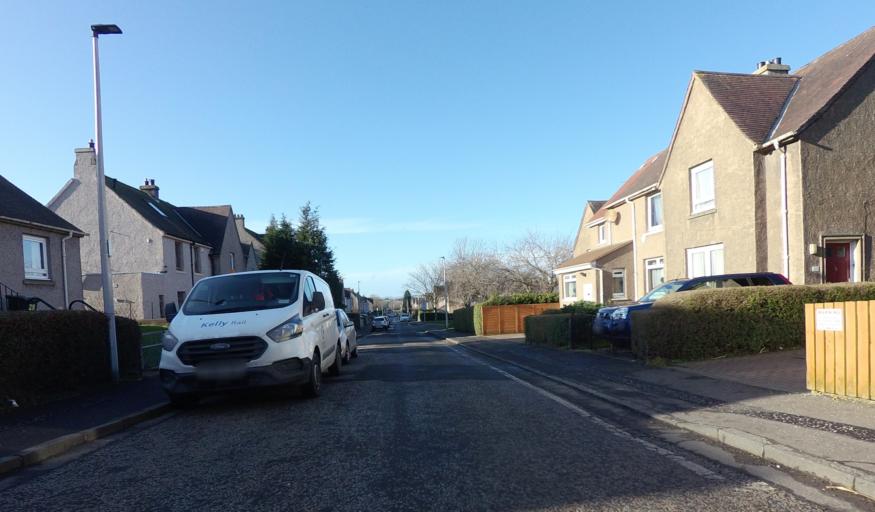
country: GB
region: Scotland
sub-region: Edinburgh
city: Colinton
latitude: 55.9591
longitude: -3.2880
